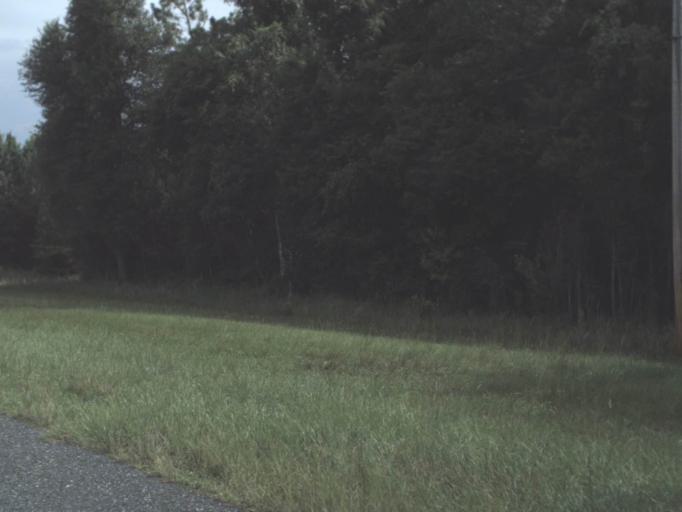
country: US
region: Florida
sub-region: Levy County
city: Inglis
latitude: 29.2104
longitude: -82.6973
